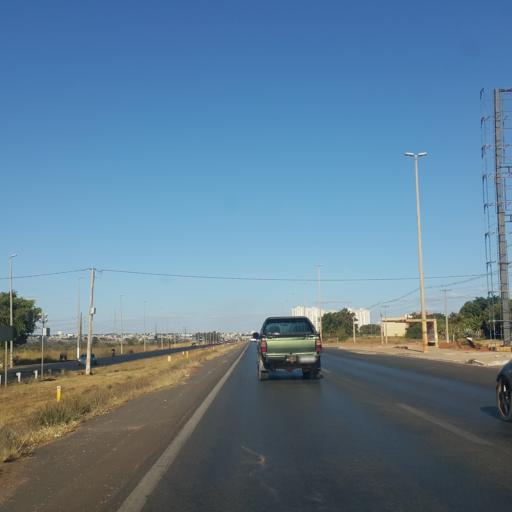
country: BR
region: Federal District
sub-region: Brasilia
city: Brasilia
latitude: -15.7914
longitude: -48.1052
